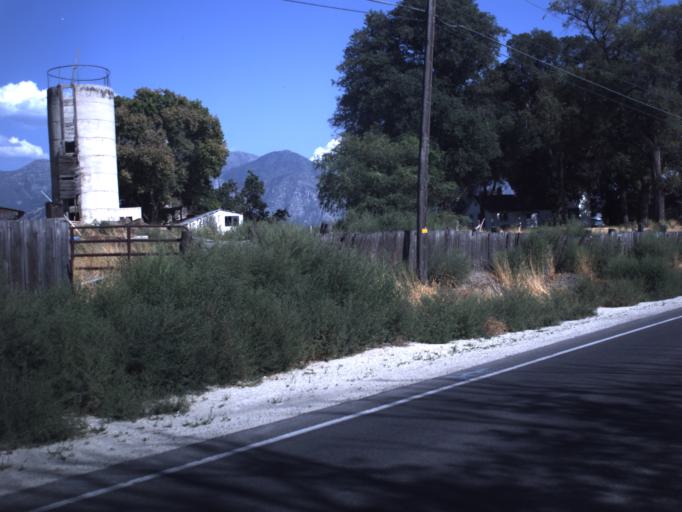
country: US
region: Utah
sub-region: Utah County
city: Orem
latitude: 40.2691
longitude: -111.7223
